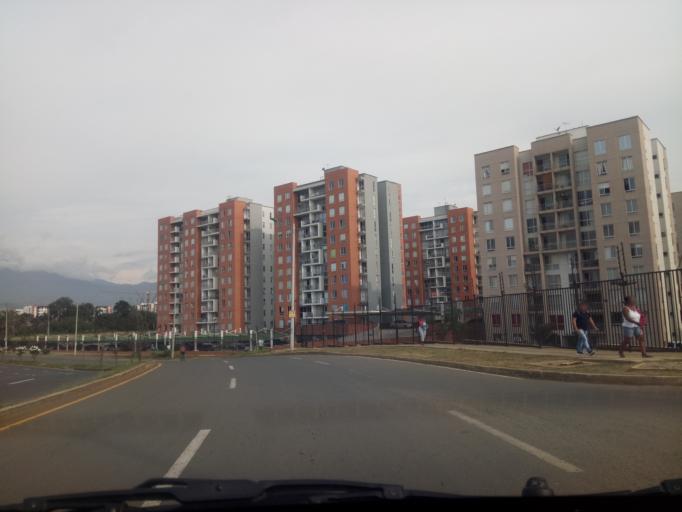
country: CO
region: Valle del Cauca
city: Cali
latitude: 3.3680
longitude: -76.5102
